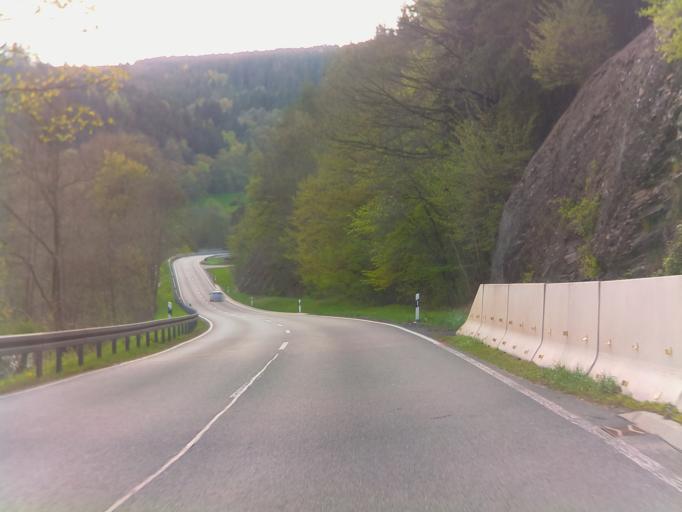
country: DE
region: Thuringia
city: Probstzella
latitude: 50.5459
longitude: 11.3567
